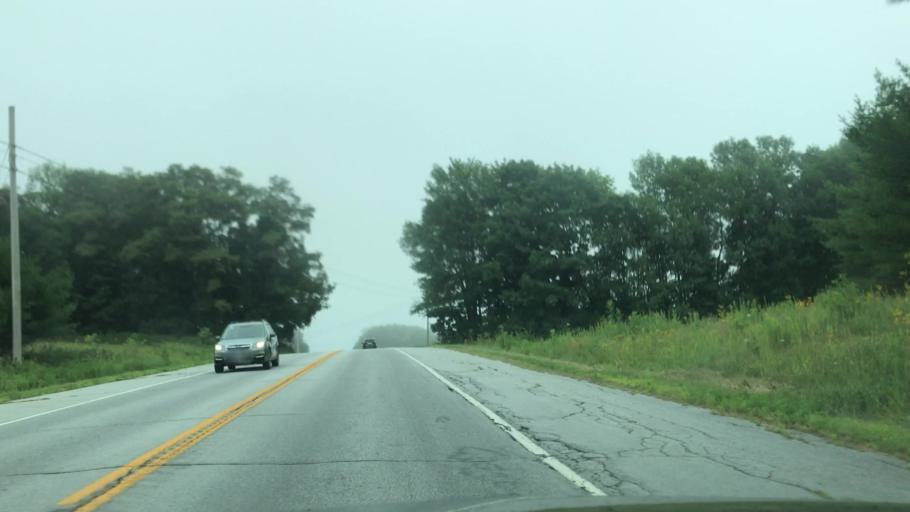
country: US
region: Maine
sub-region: Lincoln County
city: Nobleboro
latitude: 44.0962
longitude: -69.4613
